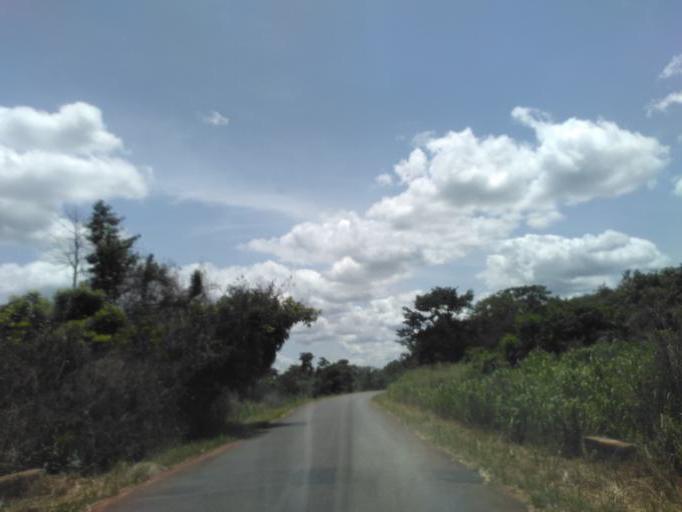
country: GH
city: Akropong
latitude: 6.1039
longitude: -0.1062
